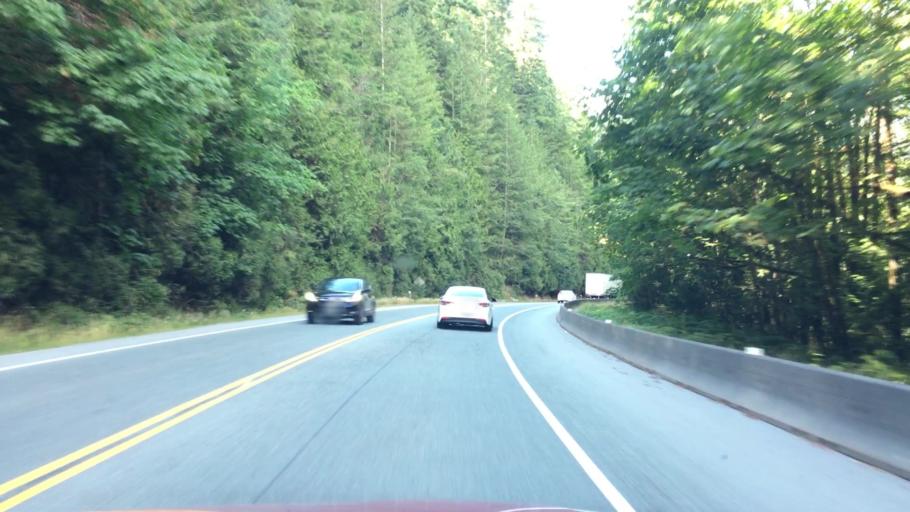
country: CA
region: British Columbia
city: Port Alberni
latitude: 49.2541
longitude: -124.6645
